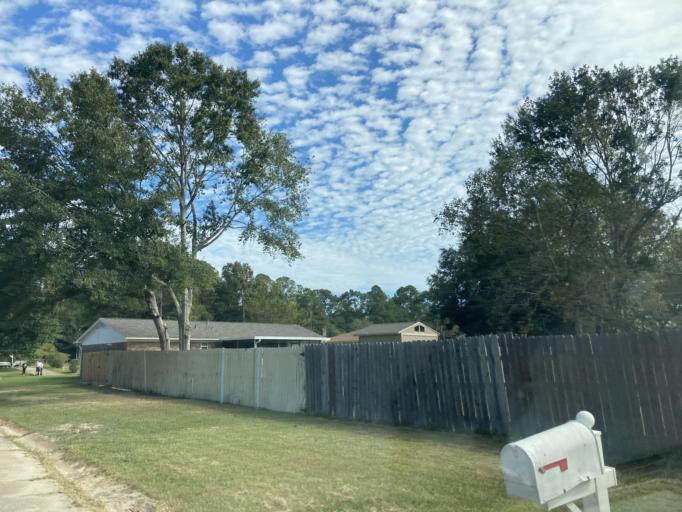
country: US
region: Mississippi
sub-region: Jackson County
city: Saint Martin
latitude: 30.4472
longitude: -88.8688
